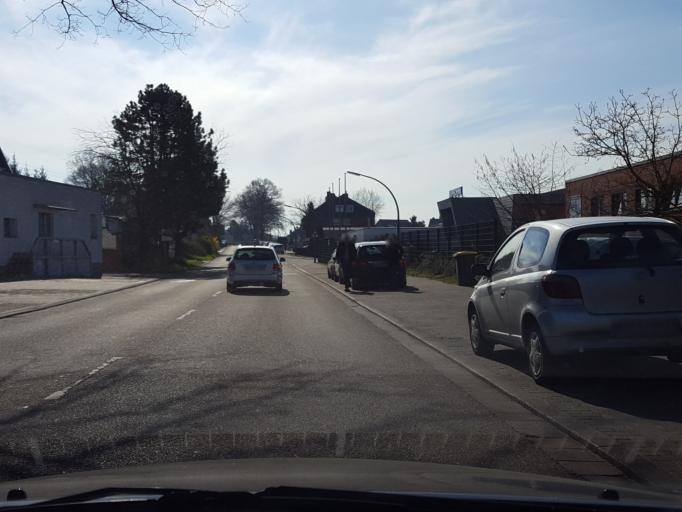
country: DE
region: North Rhine-Westphalia
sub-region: Regierungsbezirk Munster
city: Recklinghausen
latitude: 51.6717
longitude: 7.1658
